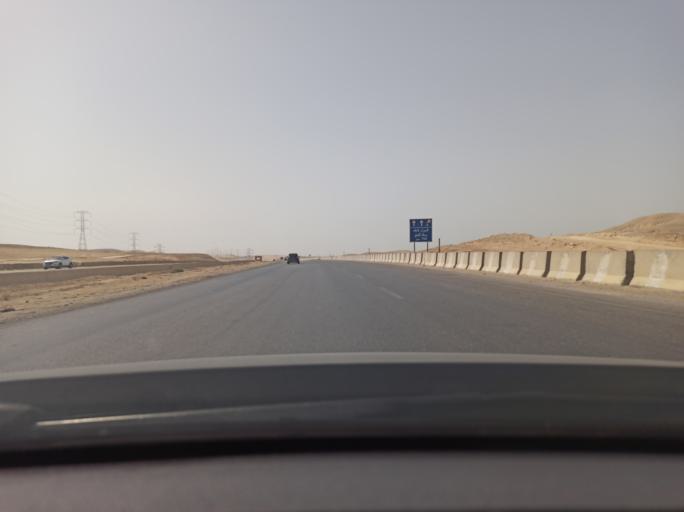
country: EG
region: Al Jizah
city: As Saff
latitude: 29.5378
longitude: 31.3885
